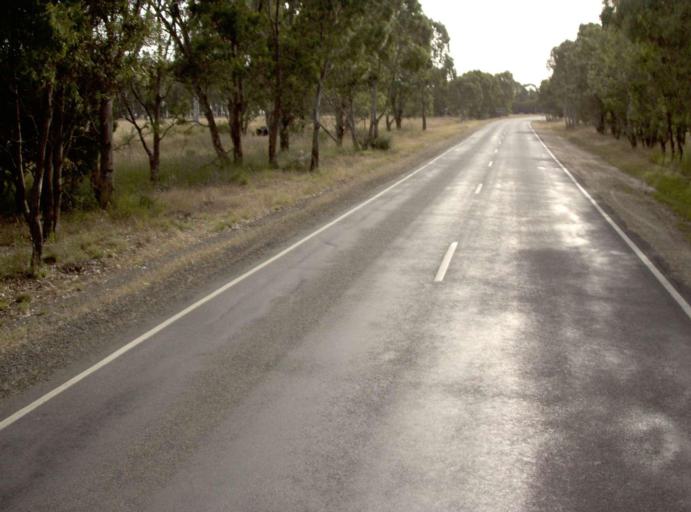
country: AU
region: Victoria
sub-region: Wellington
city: Heyfield
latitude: -38.0598
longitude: 146.6575
